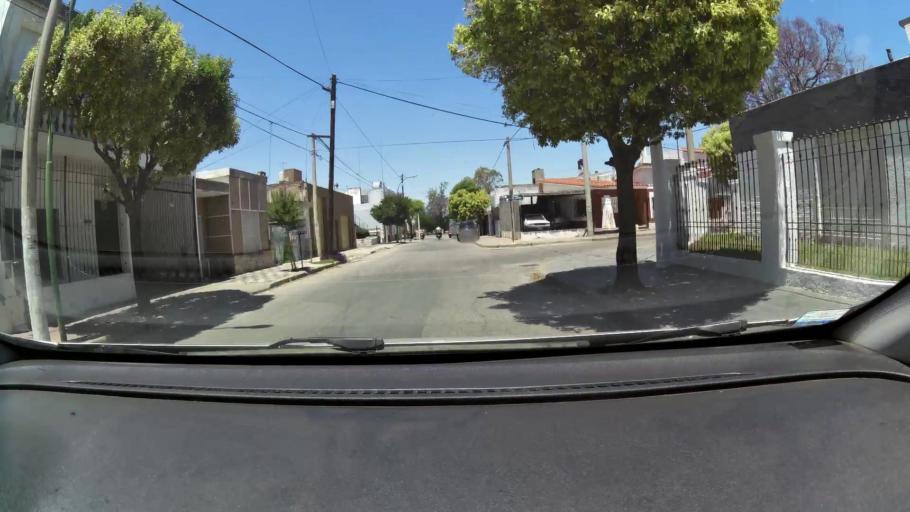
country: AR
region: Cordoba
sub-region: Departamento de Capital
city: Cordoba
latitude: -31.3888
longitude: -64.1373
